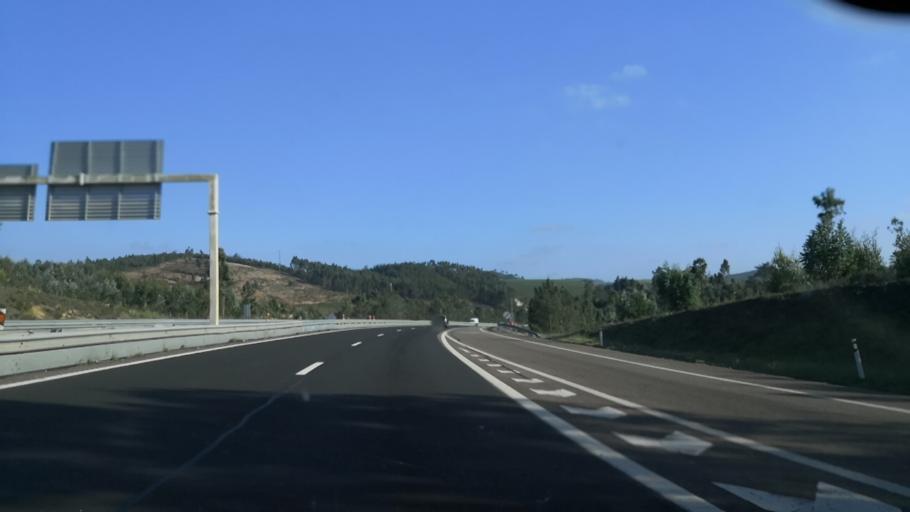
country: PT
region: Lisbon
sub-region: Torres Vedras
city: Torres Vedras
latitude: 39.1077
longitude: -9.2402
